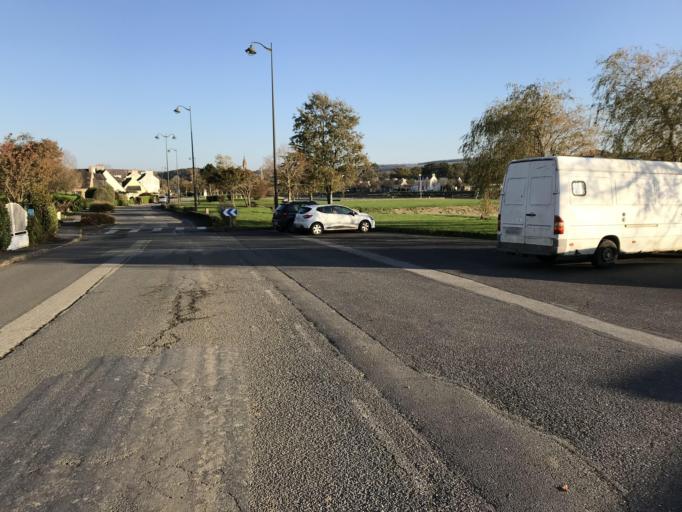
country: FR
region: Brittany
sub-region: Departement du Finistere
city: Le Faou
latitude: 48.2972
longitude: -4.1883
